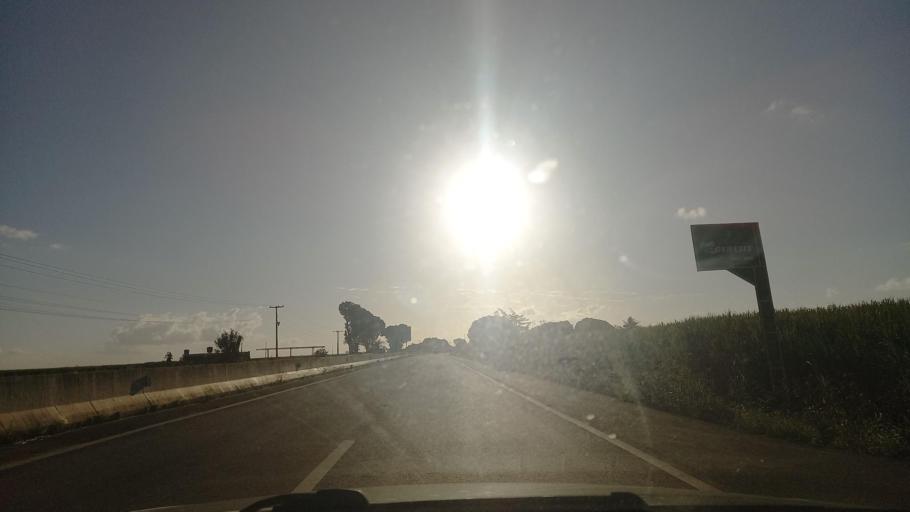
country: BR
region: Alagoas
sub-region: Campo Alegre
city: Campo Alegre
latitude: -9.7927
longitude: -36.3161
